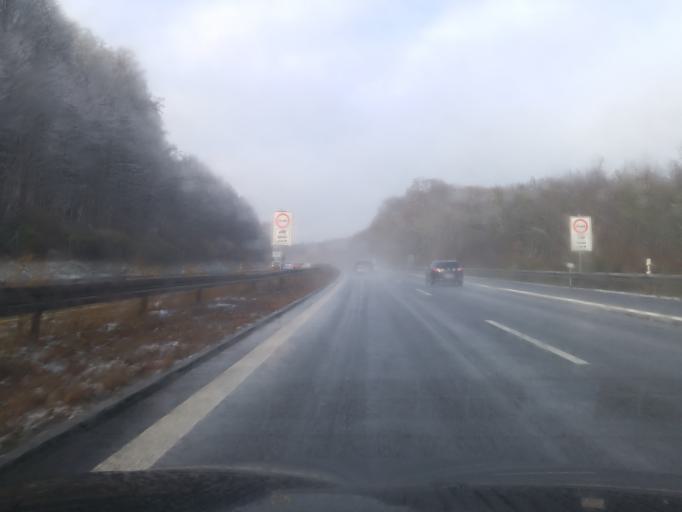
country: DE
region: Bavaria
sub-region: Regierungsbezirk Unterfranken
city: Wasserlosen
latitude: 50.0944
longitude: 9.9822
